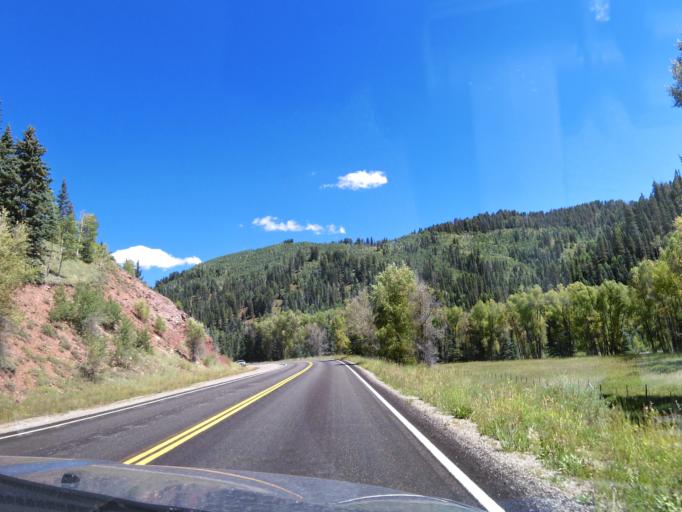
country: US
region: Colorado
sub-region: Montezuma County
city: Mancos
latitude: 37.6205
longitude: -108.0699
